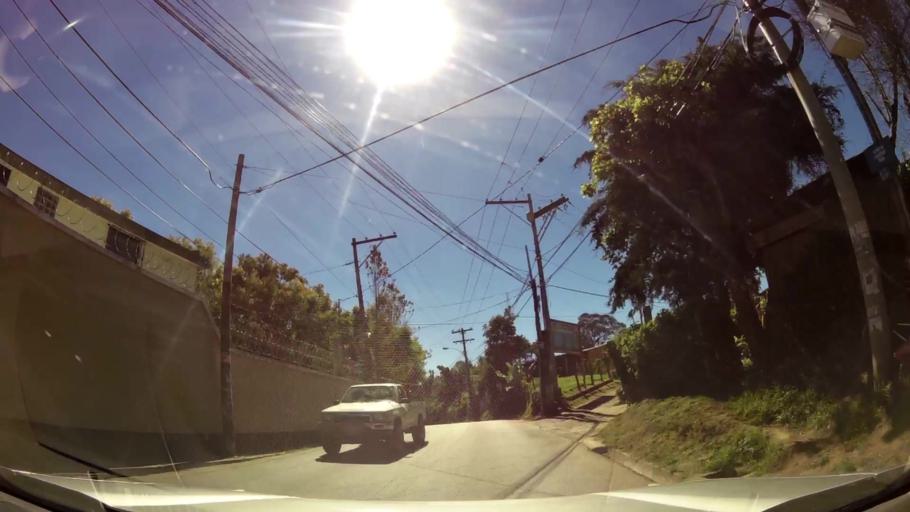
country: GT
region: Guatemala
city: San Jose Pinula
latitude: 14.5161
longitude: -90.4322
